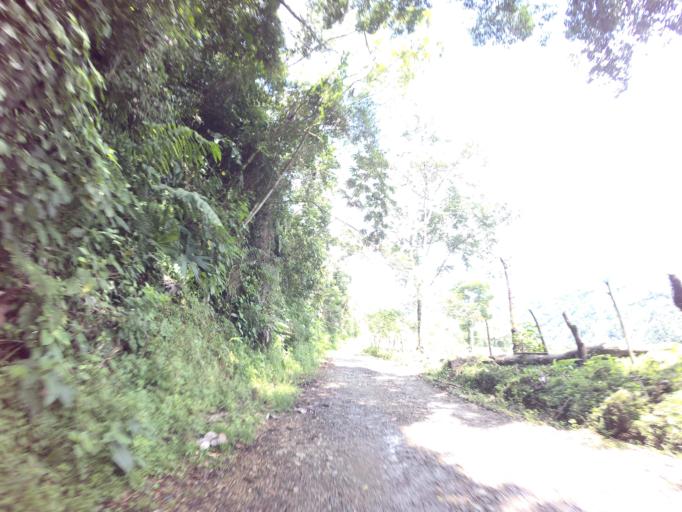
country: CO
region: Antioquia
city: Narino
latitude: 5.5155
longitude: -75.1958
